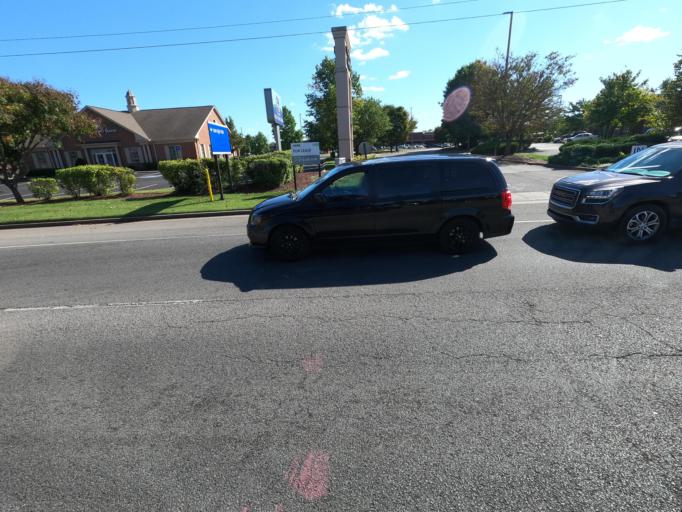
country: US
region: Tennessee
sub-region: Rutherford County
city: Murfreesboro
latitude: 35.8455
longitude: -86.4426
